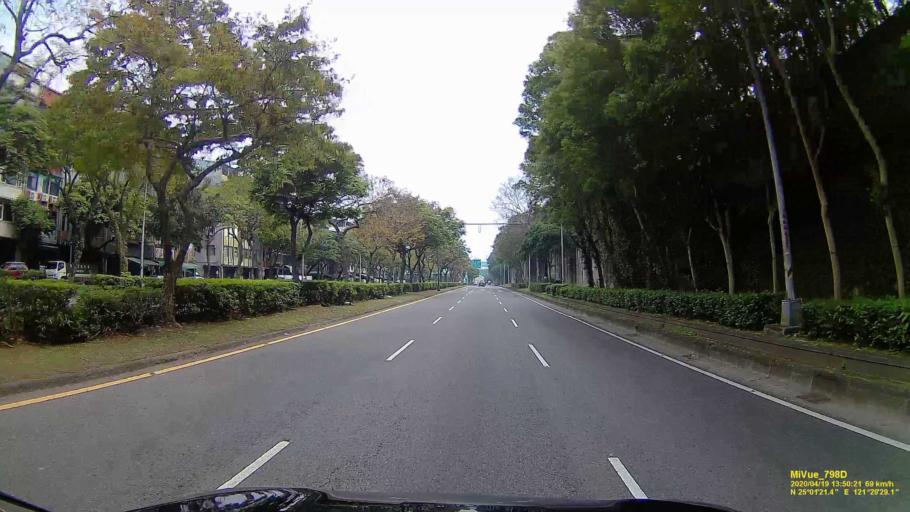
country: TW
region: Taipei
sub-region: Taipei
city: Banqiao
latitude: 25.0222
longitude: 121.4916
